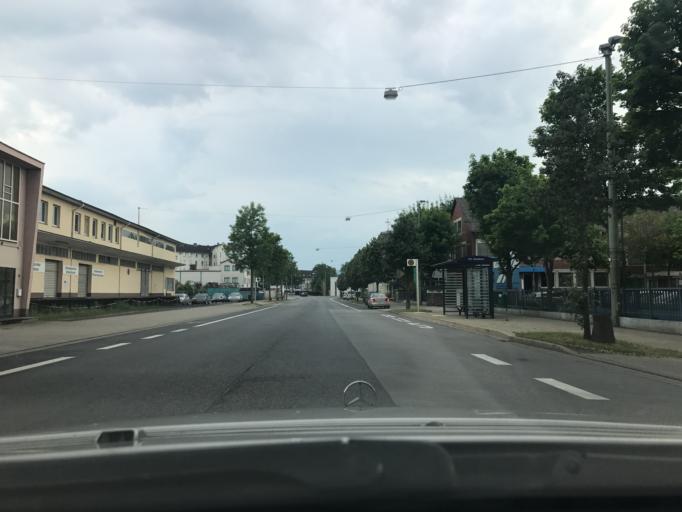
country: DE
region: Hesse
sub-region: Regierungsbezirk Kassel
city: Kassel
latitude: 51.3097
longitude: 9.5222
